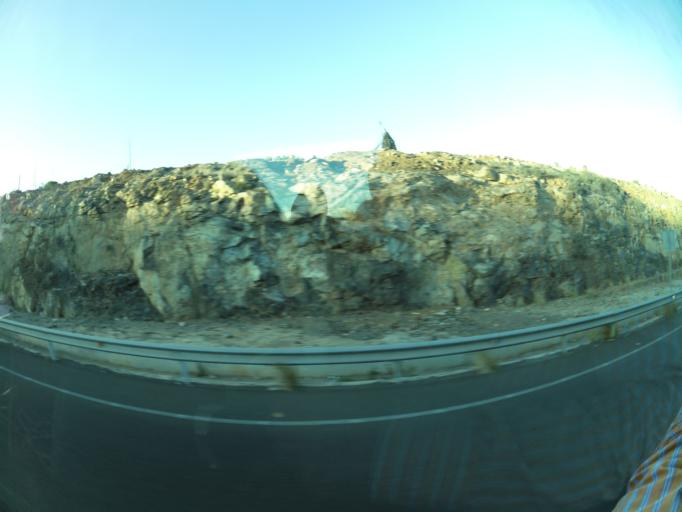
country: ES
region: Canary Islands
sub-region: Provincia de Las Palmas
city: Playa del Ingles
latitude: 27.7751
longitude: -15.5322
